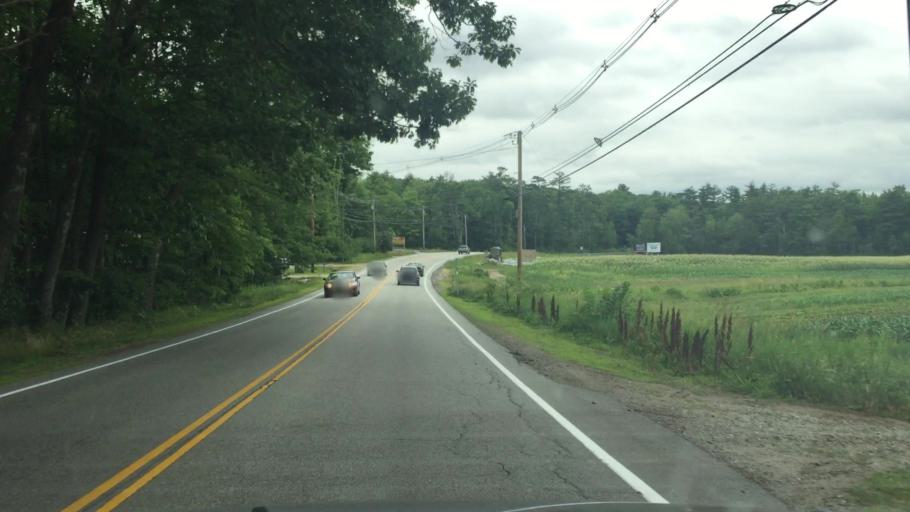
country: US
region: New Hampshire
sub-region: Carroll County
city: Center Harbor
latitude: 43.6802
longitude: -71.4705
